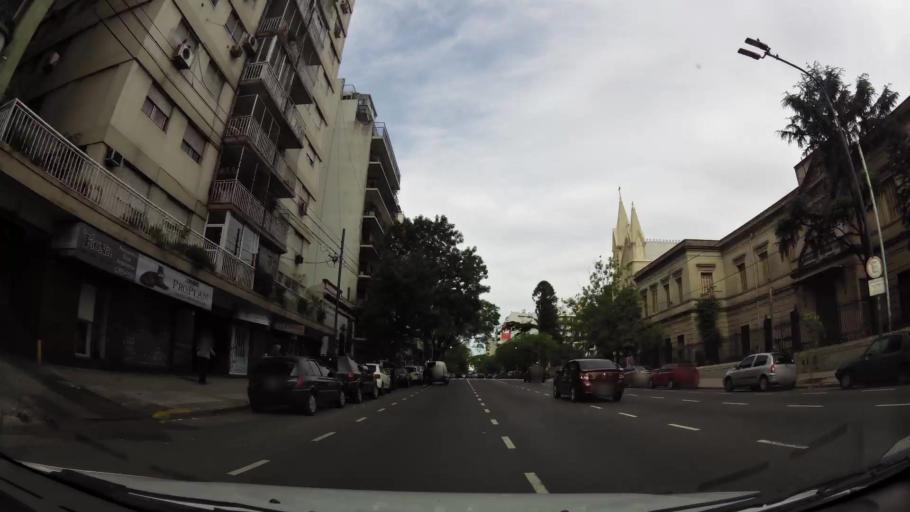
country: AR
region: Buenos Aires F.D.
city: Villa Santa Rita
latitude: -34.6324
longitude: -58.4572
